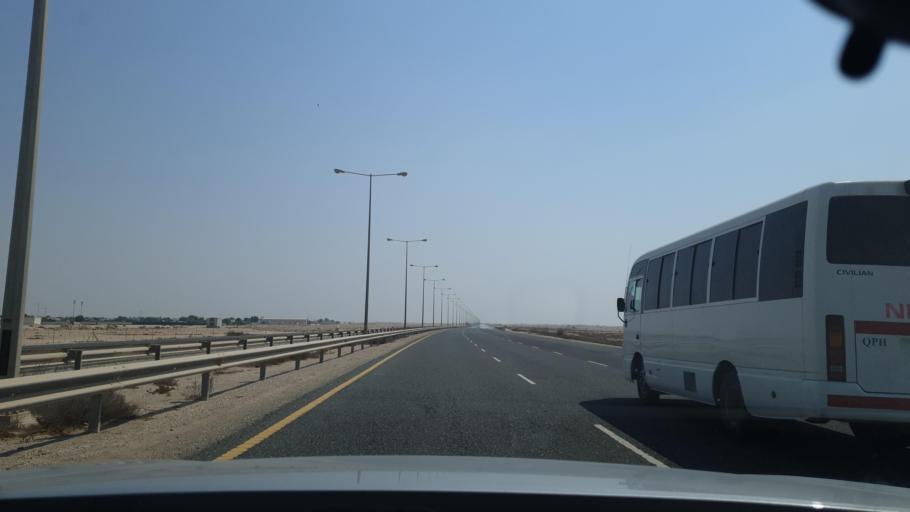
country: QA
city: Al Ghuwayriyah
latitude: 25.8188
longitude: 51.3670
